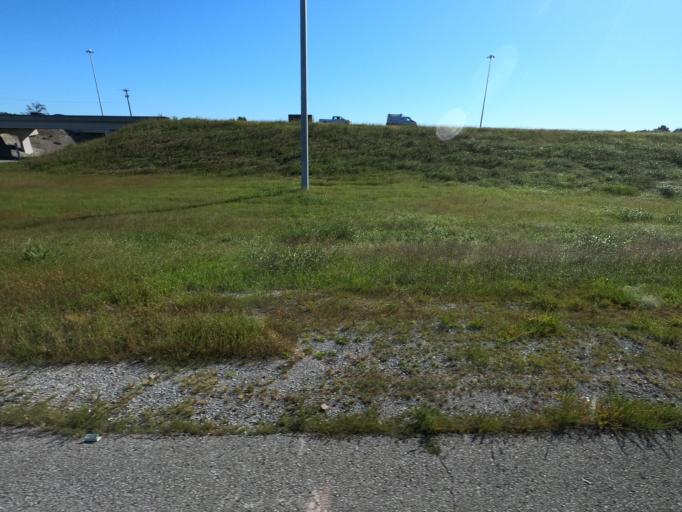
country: US
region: Tennessee
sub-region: Wilson County
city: Rural Hill
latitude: 36.1115
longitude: -86.4102
